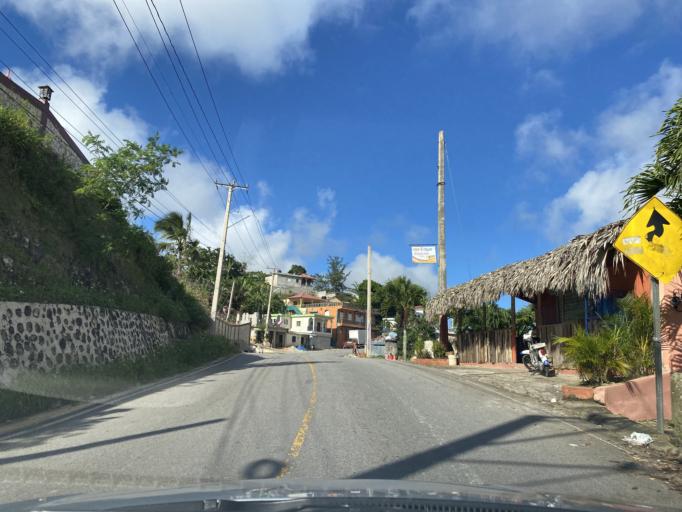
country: DO
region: Samana
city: Sanchez
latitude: 19.2568
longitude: -69.5711
